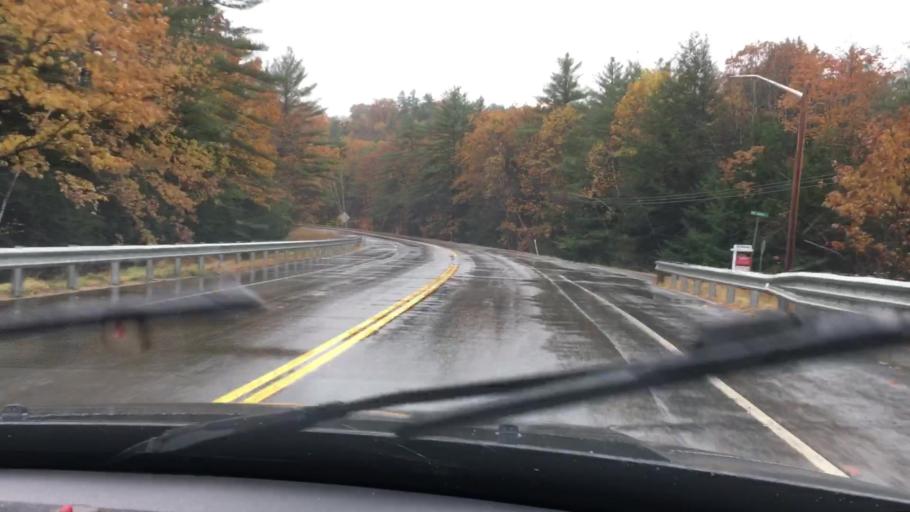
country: US
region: New Hampshire
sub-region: Grafton County
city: Ashland
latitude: 43.7184
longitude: -71.6231
